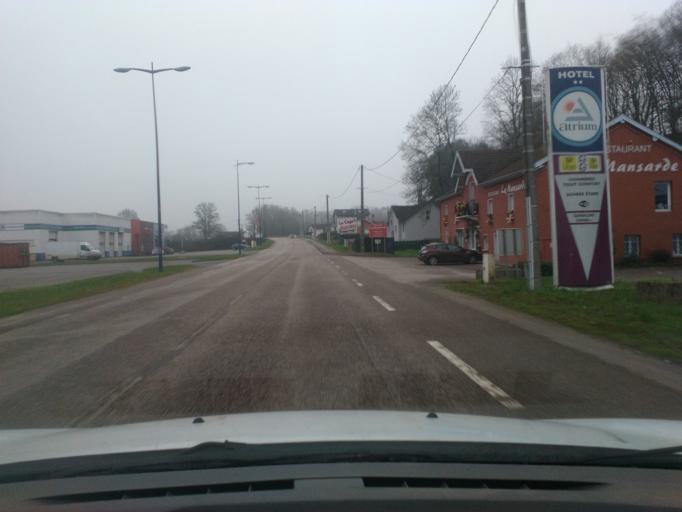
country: FR
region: Lorraine
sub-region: Departement des Vosges
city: Golbey
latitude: 48.2118
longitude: 6.4401
